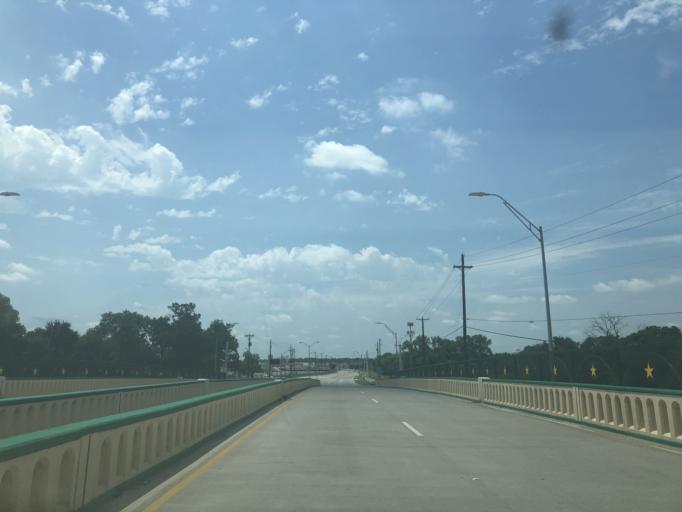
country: US
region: Texas
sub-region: Dallas County
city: Irving
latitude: 32.7734
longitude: -96.9600
